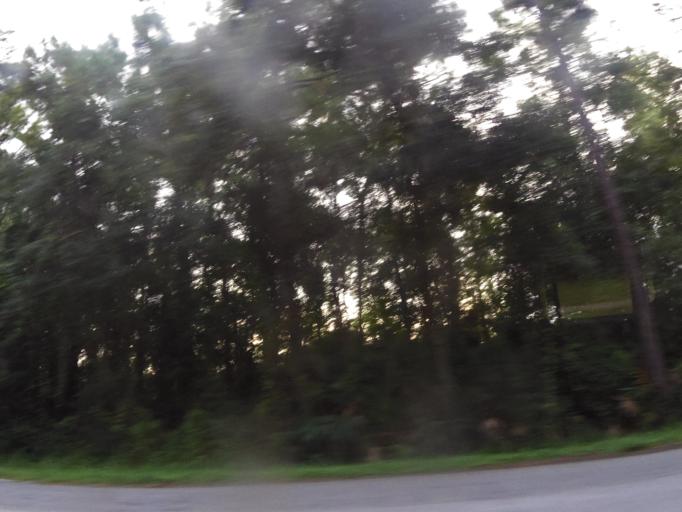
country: US
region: Florida
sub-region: Clay County
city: Bellair-Meadowbrook Terrace
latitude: 30.2686
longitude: -81.7813
